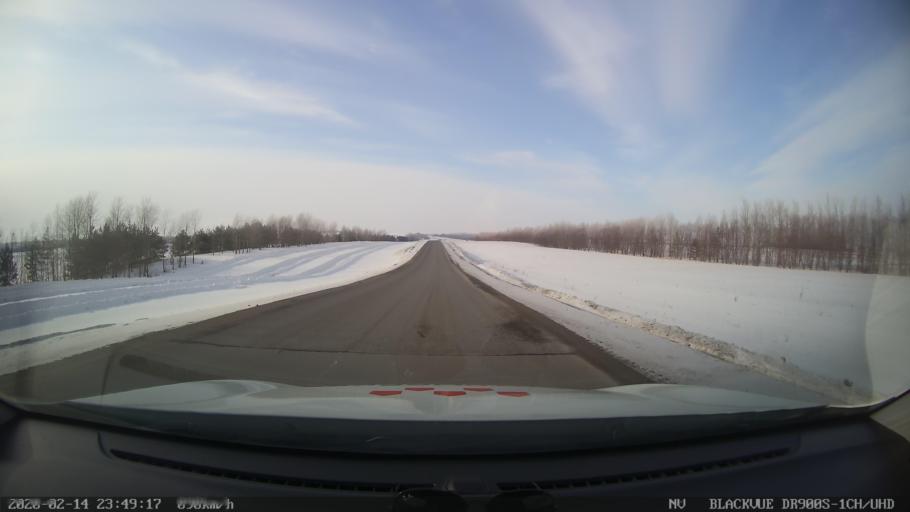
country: RU
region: Tatarstan
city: Kuybyshevskiy Zaton
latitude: 55.2526
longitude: 49.1857
